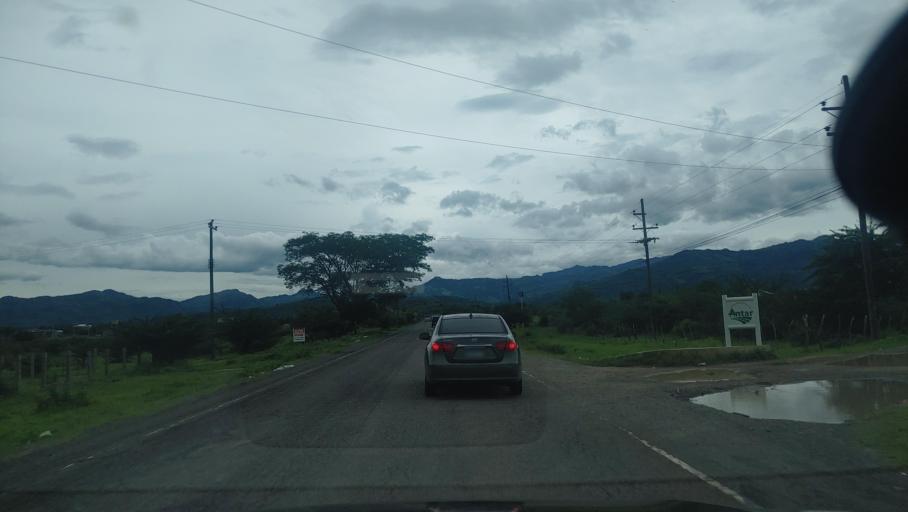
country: HN
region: Choluteca
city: Santa Ana de Yusguare
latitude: 13.3446
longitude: -87.1200
